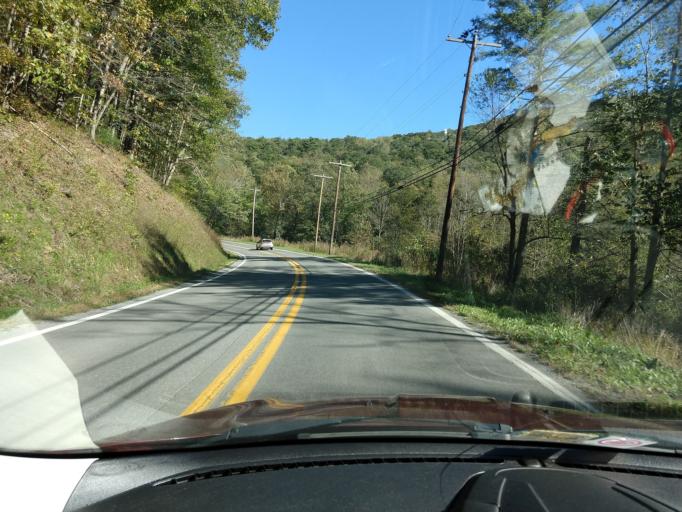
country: US
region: West Virginia
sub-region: Pocahontas County
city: Marlinton
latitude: 38.2092
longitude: -80.0515
